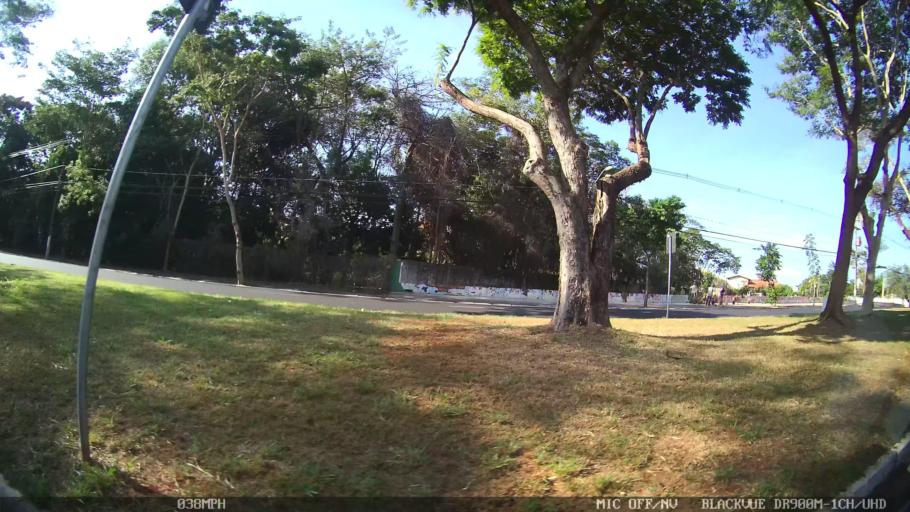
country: BR
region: Sao Paulo
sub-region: Ribeirao Preto
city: Ribeirao Preto
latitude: -21.1987
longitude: -47.7925
